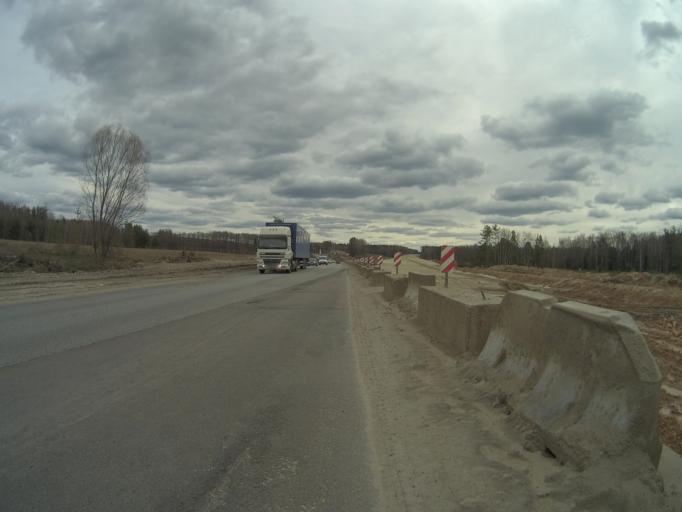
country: RU
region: Vladimir
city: Kommunar
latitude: 56.0665
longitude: 40.5009
